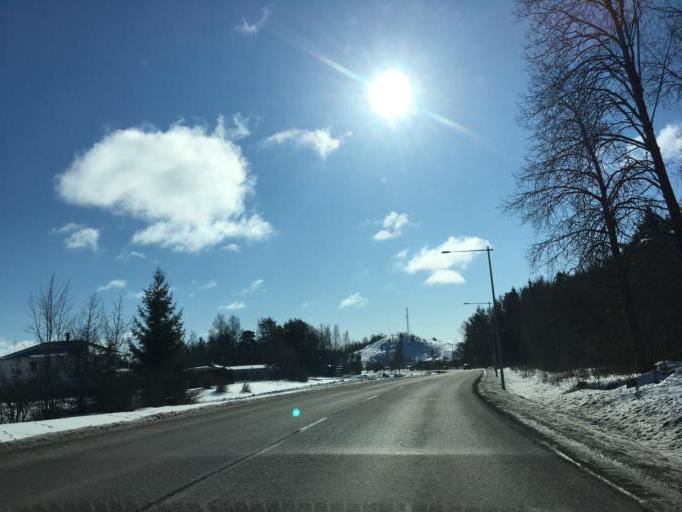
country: SE
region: Vaestmanland
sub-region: Vasteras
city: Vasteras
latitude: 59.6311
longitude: 16.4783
